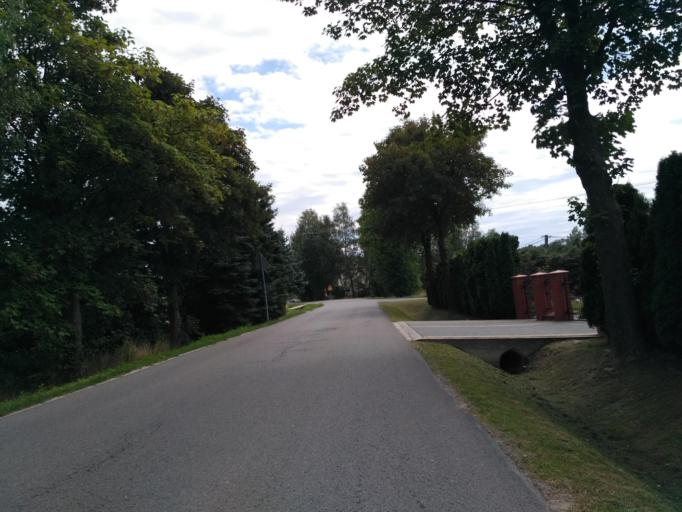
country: PL
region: Subcarpathian Voivodeship
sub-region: Powiat rzeszowski
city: Chmielnik
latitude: 49.9527
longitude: 22.1366
